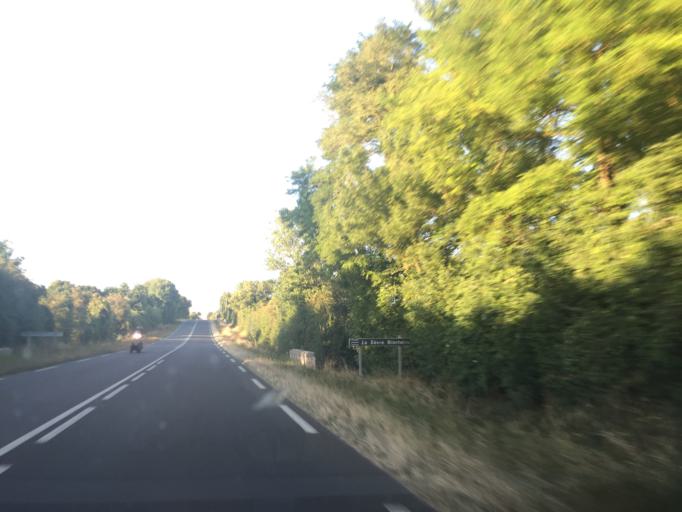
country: FR
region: Poitou-Charentes
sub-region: Departement des Deux-Sevres
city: Lezay
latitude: 46.3161
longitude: -0.0414
